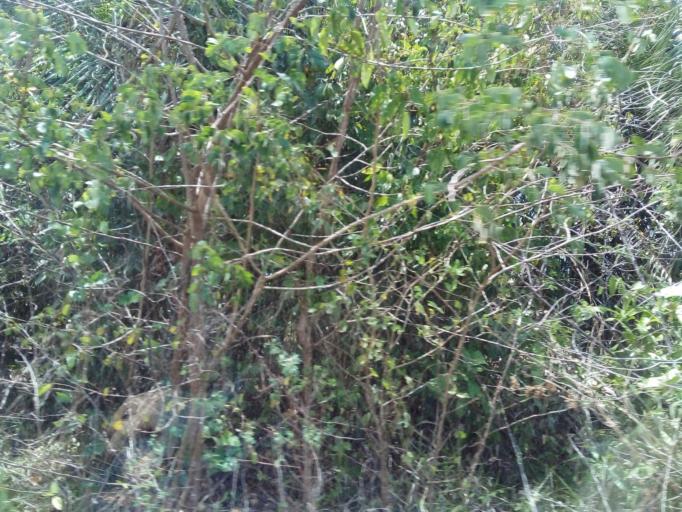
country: BR
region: Maranhao
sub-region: Itapecuru Mirim
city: Itapecuru Mirim
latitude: -3.1338
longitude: -44.3358
